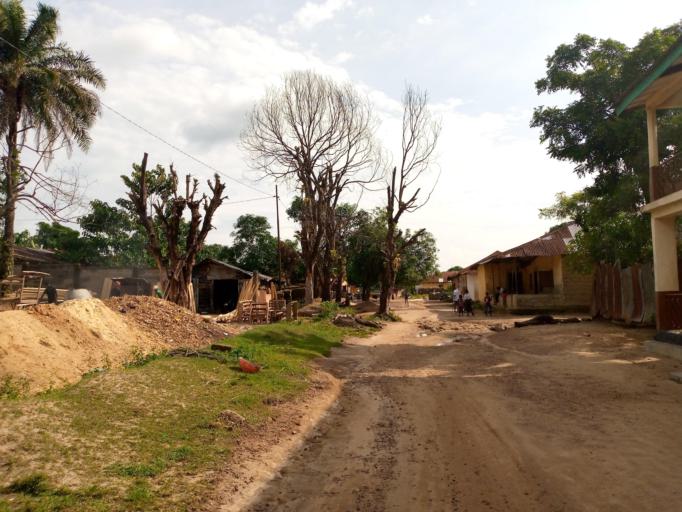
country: SL
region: Northern Province
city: Magburaka
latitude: 8.7226
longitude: -11.9486
